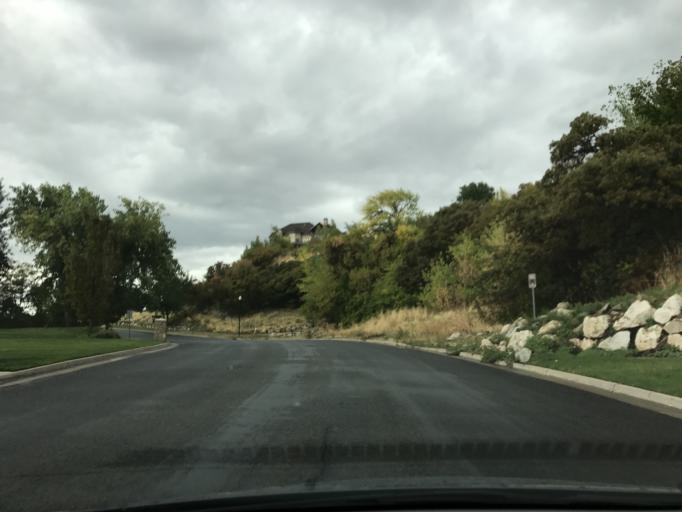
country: US
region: Utah
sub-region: Davis County
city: Fruit Heights
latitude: 41.0124
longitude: -111.8970
